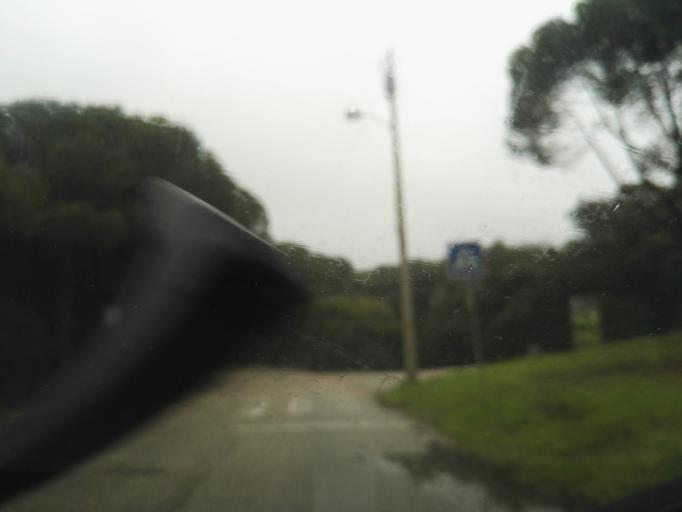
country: PT
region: Lisbon
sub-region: Odivelas
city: Pontinha
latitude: 38.7395
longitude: -9.1861
